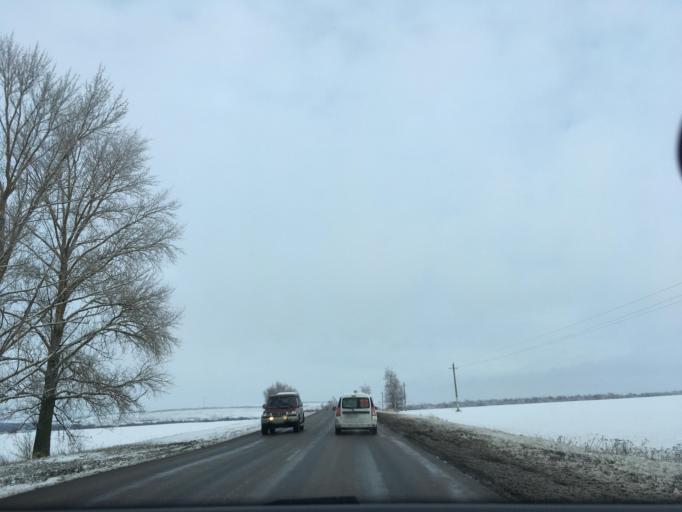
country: UA
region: Luhansk
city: Lozno-Oleksandrivka
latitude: 49.9530
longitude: 38.9585
